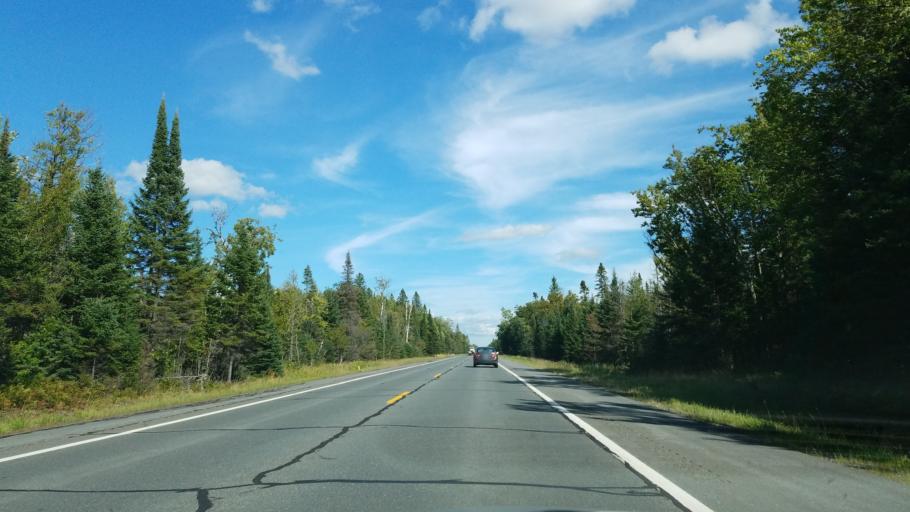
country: US
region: Michigan
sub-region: Baraga County
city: L'Anse
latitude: 46.5788
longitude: -88.4288
